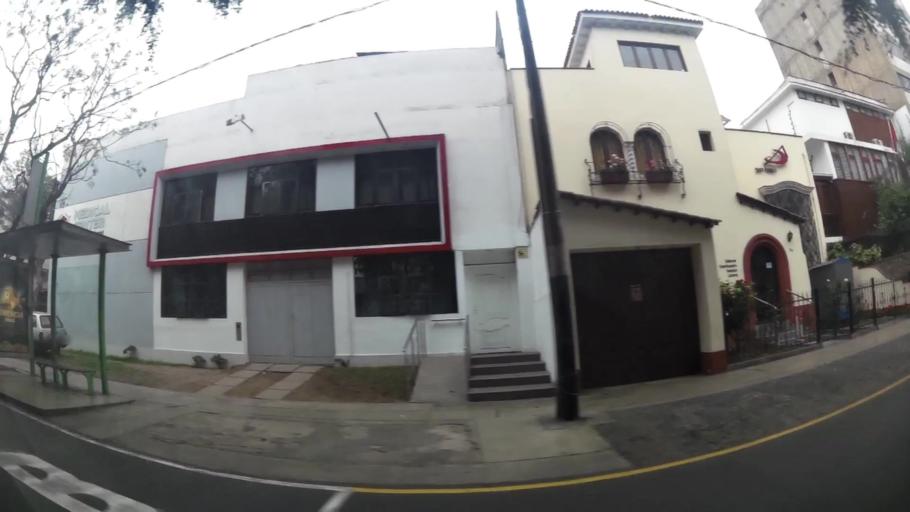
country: PE
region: Lima
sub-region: Lima
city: Surco
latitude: -12.1346
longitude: -77.0259
